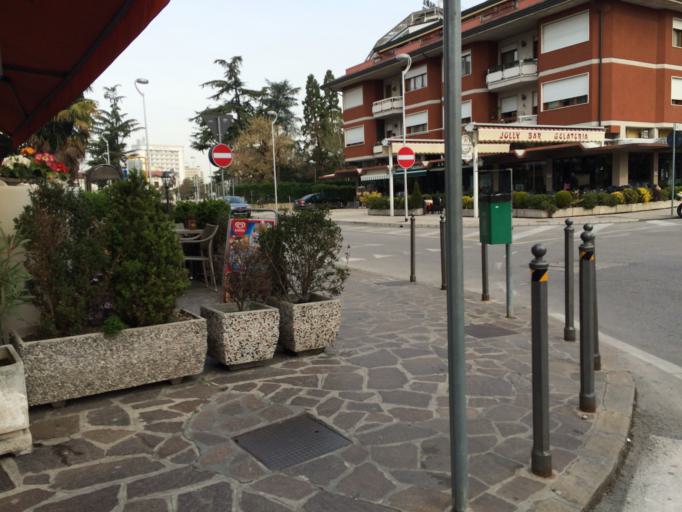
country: IT
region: Veneto
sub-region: Provincia di Padova
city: Abano Terme
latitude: 45.3510
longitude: 11.7879
